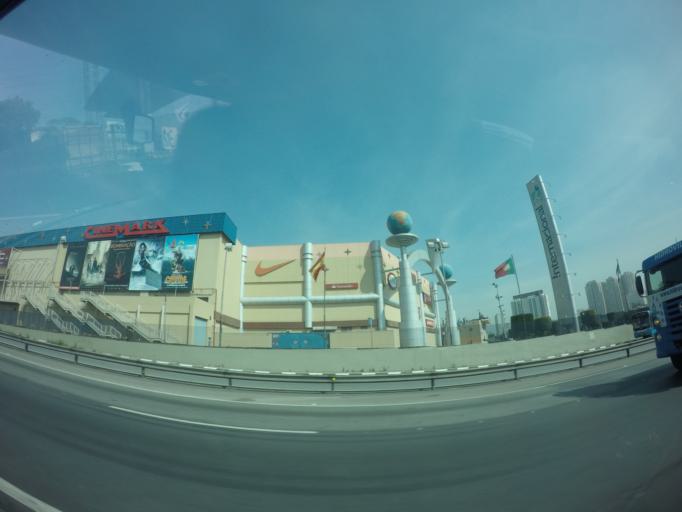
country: BR
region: Sao Paulo
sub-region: Guarulhos
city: Guarulhos
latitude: -23.4899
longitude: -46.5481
